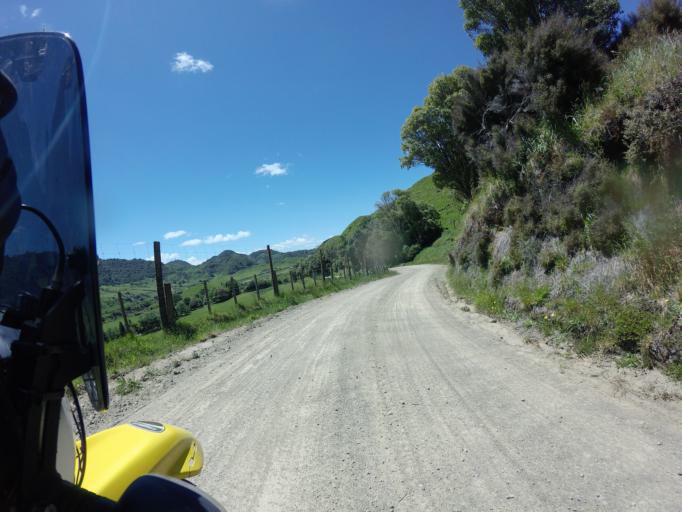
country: NZ
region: Bay of Plenty
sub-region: Opotiki District
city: Opotiki
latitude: -38.4008
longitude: 177.4568
